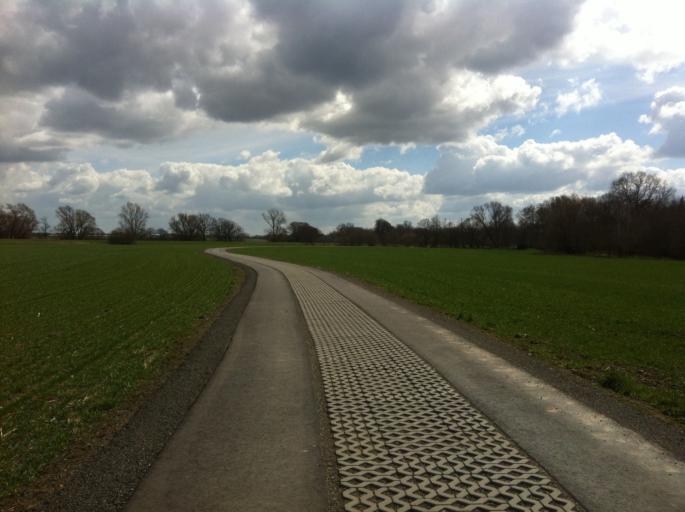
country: DE
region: Saxony
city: Trebsen
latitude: 51.3026
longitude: 12.7505
